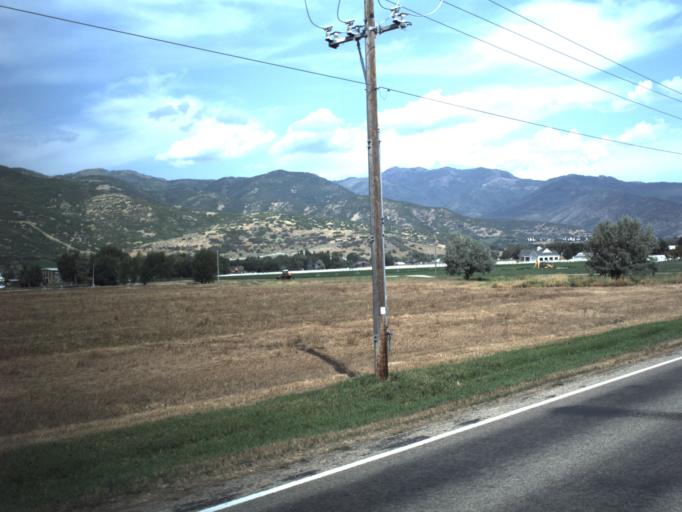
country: US
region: Utah
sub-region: Wasatch County
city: Midway
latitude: 40.4909
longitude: -111.4720
